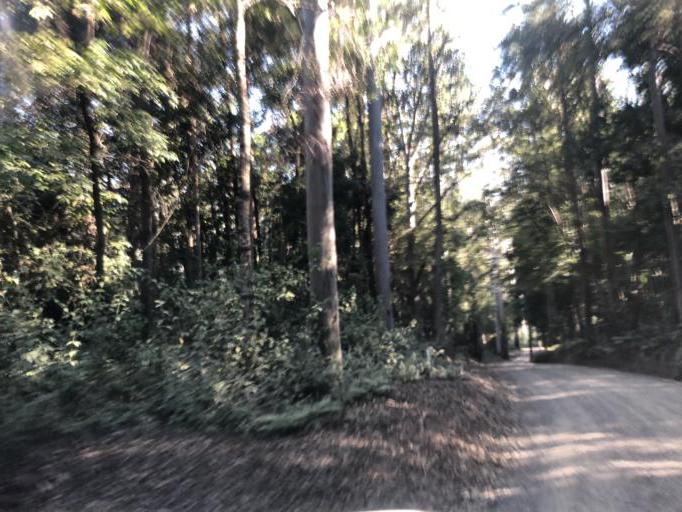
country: AU
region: New South Wales
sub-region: Bellingen
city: Bellingen
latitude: -30.4370
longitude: 152.8317
